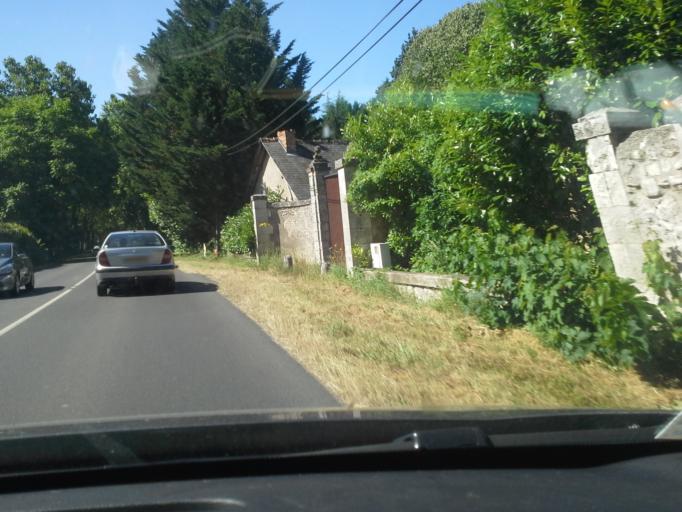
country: FR
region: Centre
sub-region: Departement du Loir-et-Cher
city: Cellettes
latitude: 47.5177
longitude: 1.3965
